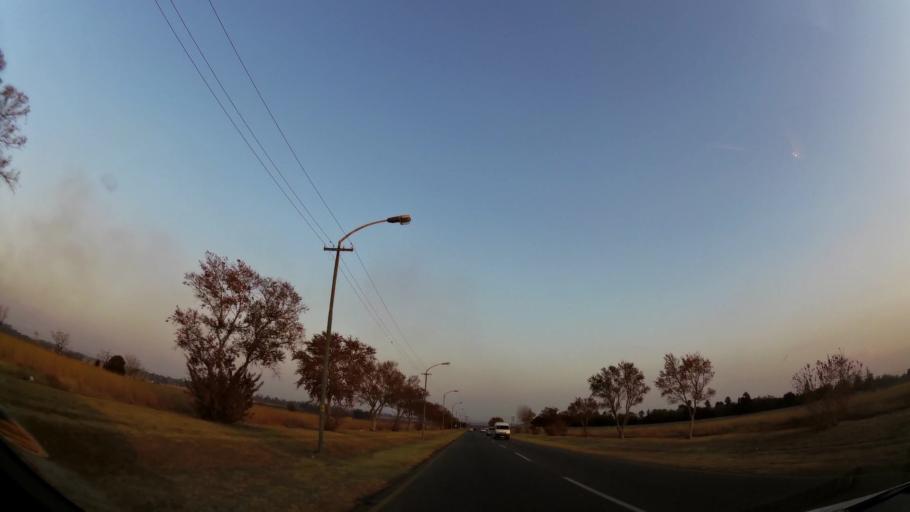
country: ZA
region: Gauteng
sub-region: Ekurhuleni Metropolitan Municipality
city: Springs
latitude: -26.3204
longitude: 28.4489
